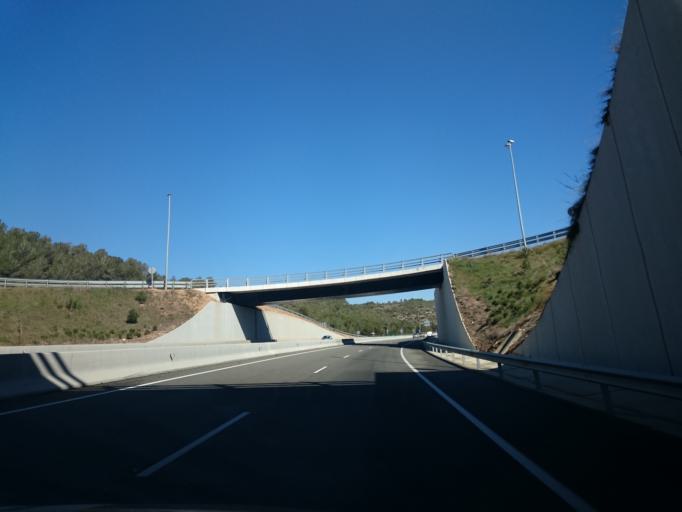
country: ES
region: Catalonia
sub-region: Provincia de Barcelona
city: Sant Pere de Ribes
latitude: 41.2907
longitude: 1.7251
